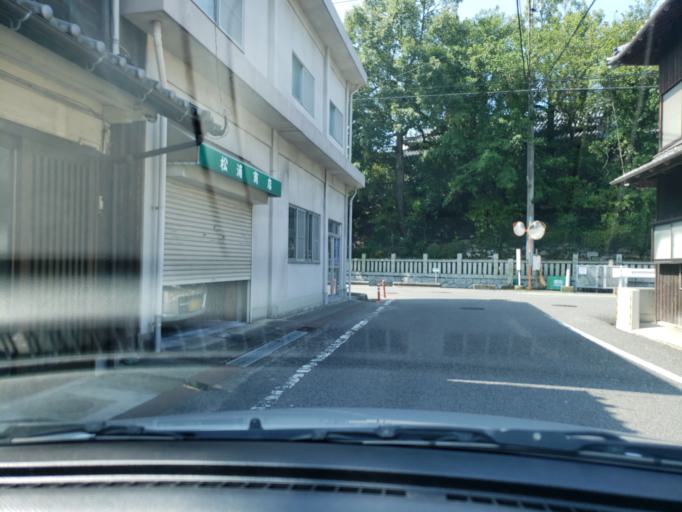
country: JP
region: Ehime
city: Hojo
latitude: 34.1063
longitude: 132.9670
